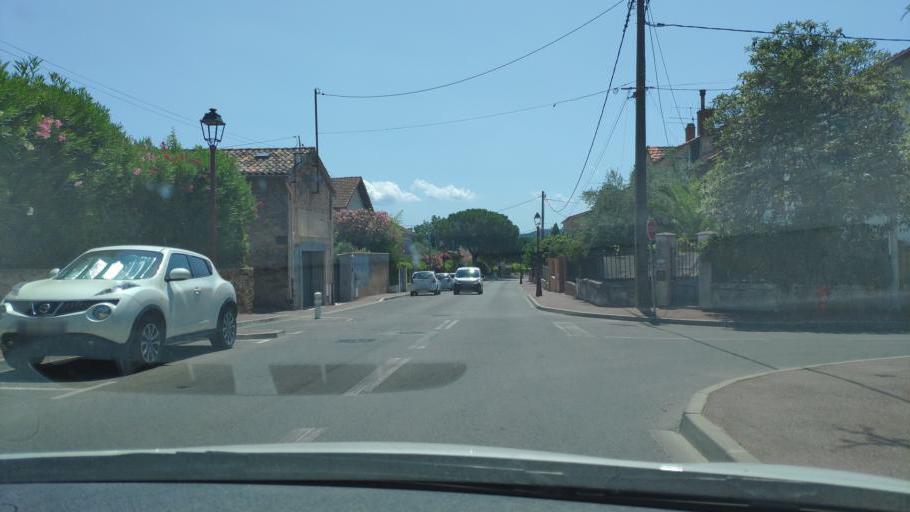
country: FR
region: Provence-Alpes-Cote d'Azur
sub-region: Departement du Var
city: Les Arcs
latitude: 43.4587
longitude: 6.4806
